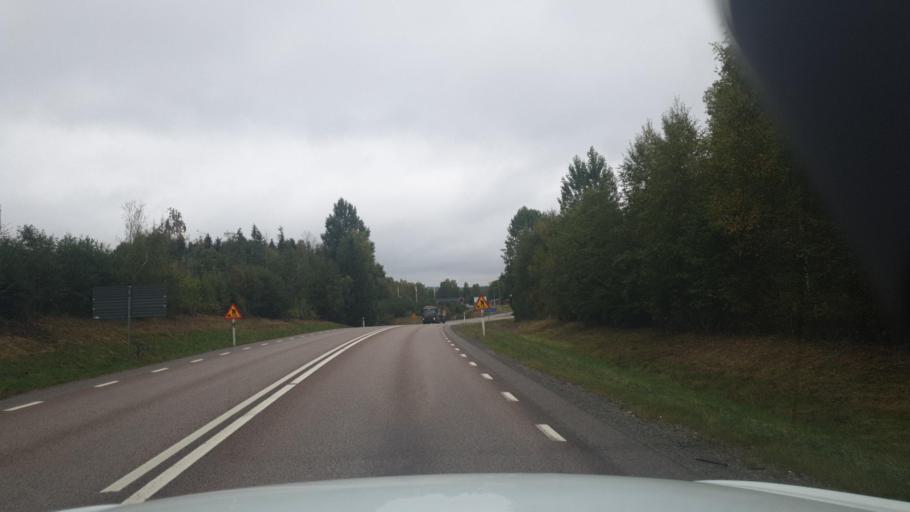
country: SE
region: Vaermland
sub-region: Sunne Kommun
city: Sunne
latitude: 59.7889
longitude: 13.0967
